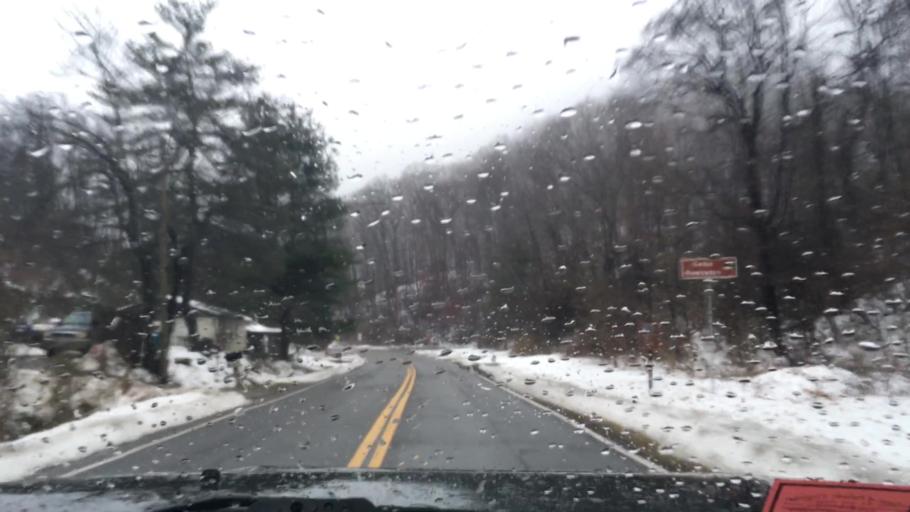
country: US
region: Virginia
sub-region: Pulaski County
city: Pulaski
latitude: 37.0292
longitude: -80.7251
